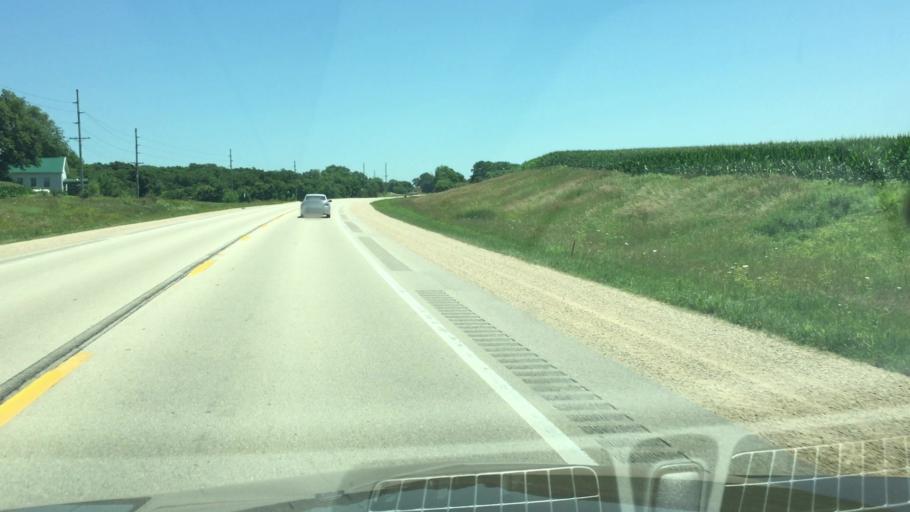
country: US
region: Iowa
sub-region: Jackson County
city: Maquoketa
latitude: 42.0642
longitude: -90.7644
